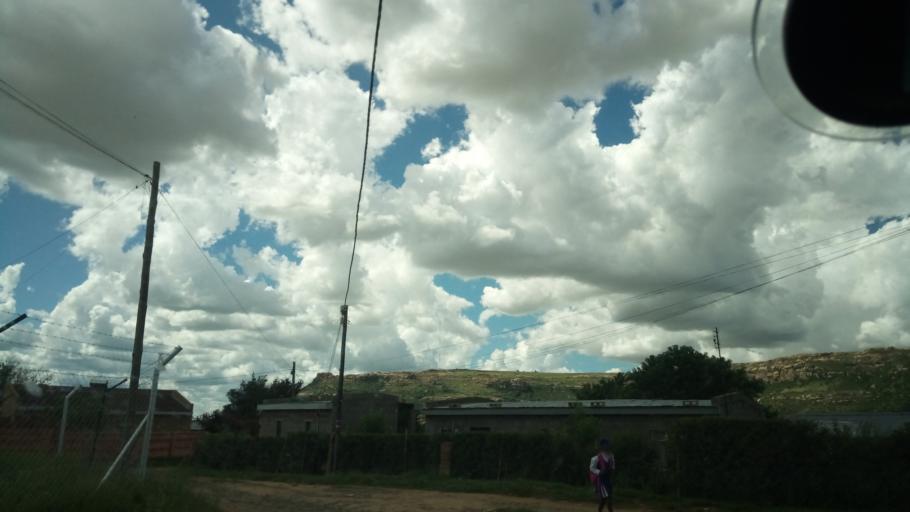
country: LS
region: Maseru
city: Maseru
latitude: -29.3527
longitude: 27.5364
